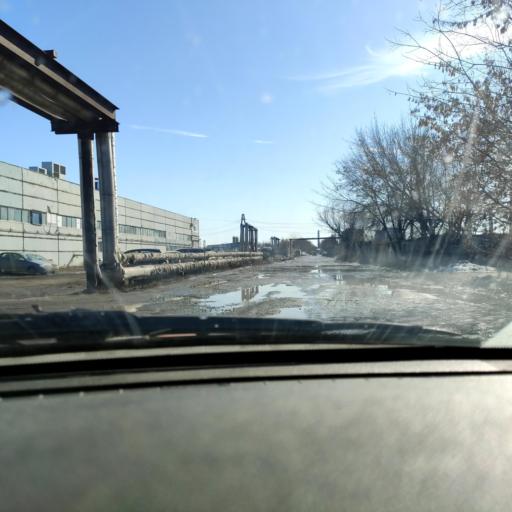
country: RU
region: Samara
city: Tol'yatti
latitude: 53.5881
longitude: 49.2580
